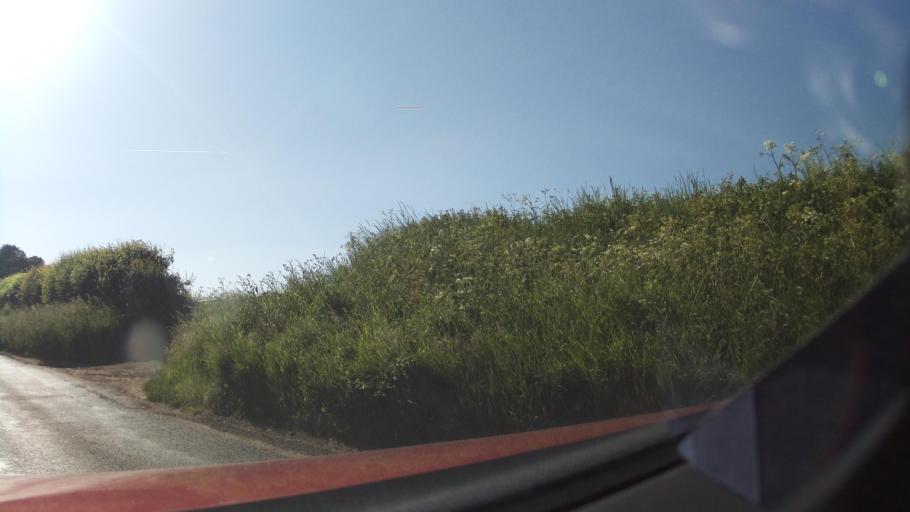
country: GB
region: England
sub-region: Dorset
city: Sherborne
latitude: 50.9391
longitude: -2.5559
